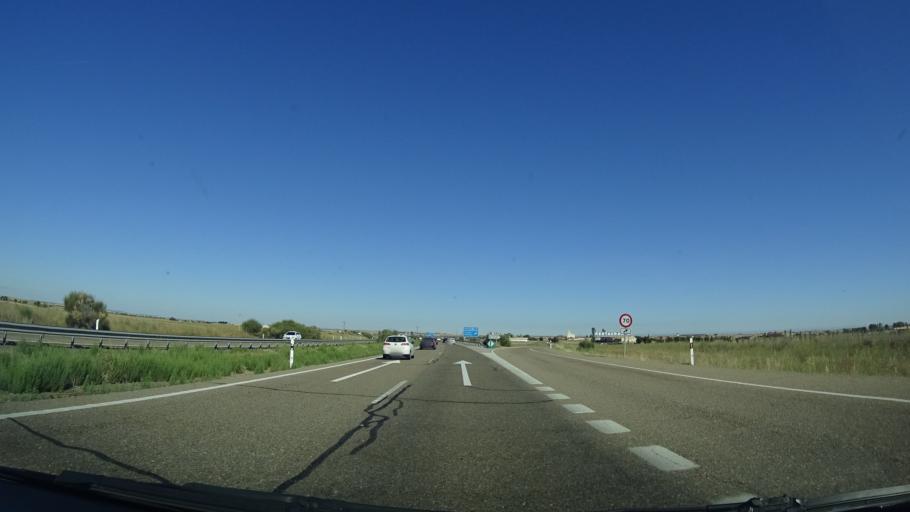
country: ES
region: Castille and Leon
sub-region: Provincia de Zamora
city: Villalpando
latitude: 41.8502
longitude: -5.4034
